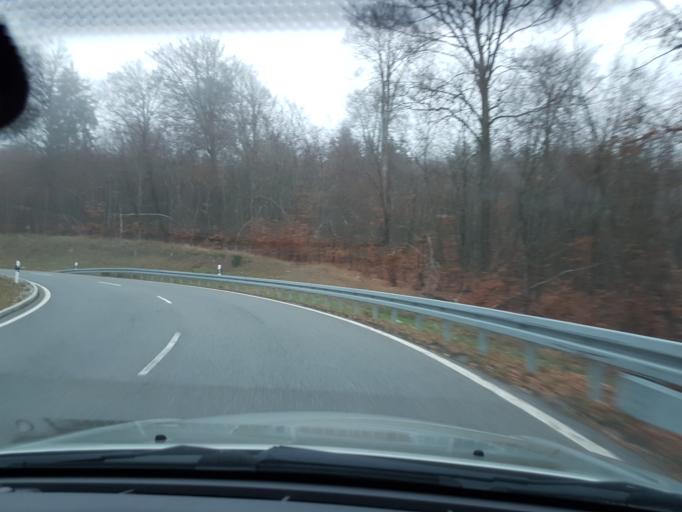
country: DE
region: Hesse
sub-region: Regierungsbezirk Darmstadt
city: Kiedrich
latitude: 50.0746
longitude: 8.0557
